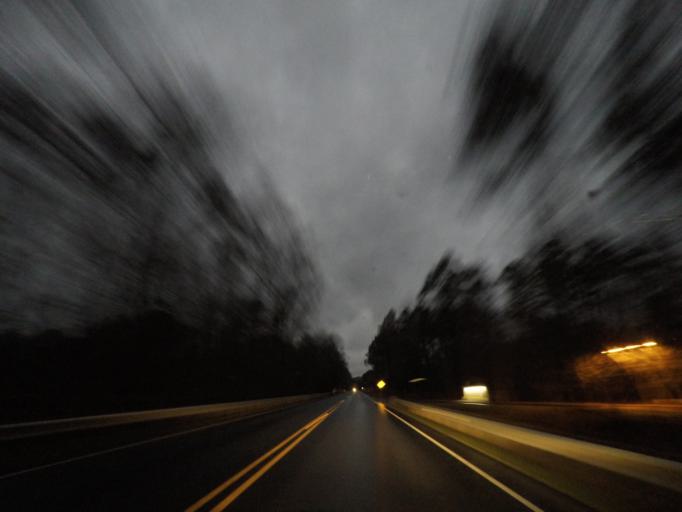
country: US
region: North Carolina
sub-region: Orange County
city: Hillsborough
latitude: 36.0451
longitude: -79.0208
